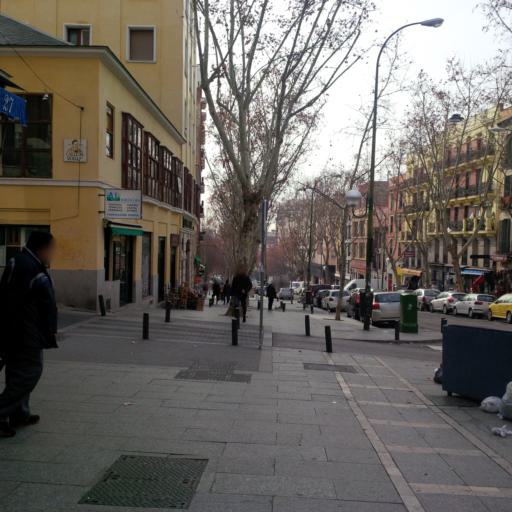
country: ES
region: Madrid
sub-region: Provincia de Madrid
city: Madrid
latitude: 40.4081
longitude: -3.7072
